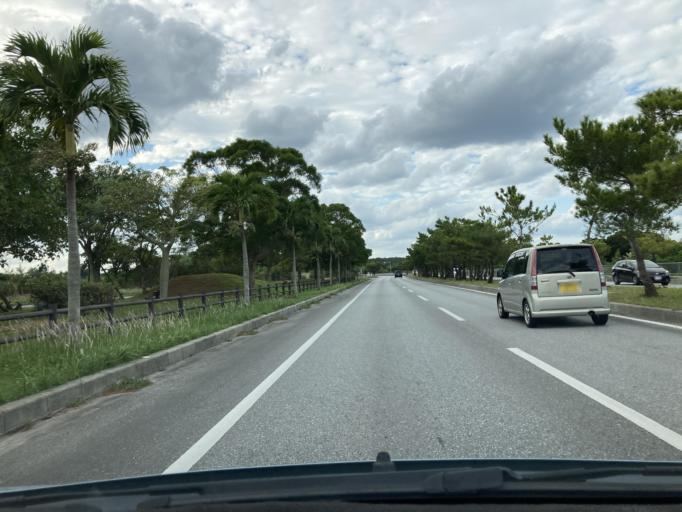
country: JP
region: Okinawa
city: Okinawa
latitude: 26.3669
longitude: 127.7870
